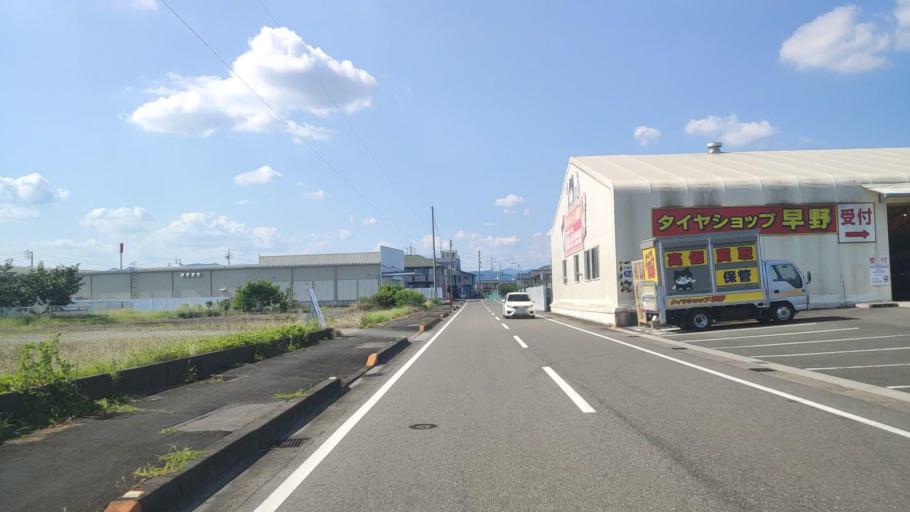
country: JP
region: Gifu
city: Godo
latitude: 35.4486
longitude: 136.6764
